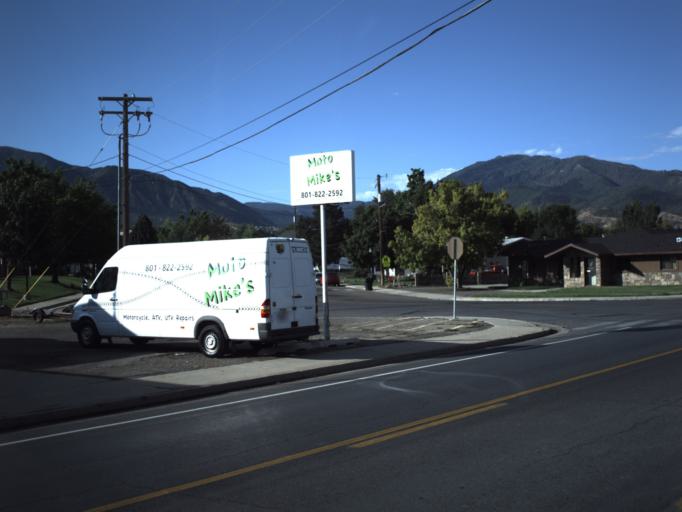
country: US
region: Utah
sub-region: Utah County
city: Salem
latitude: 40.0546
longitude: -111.6773
